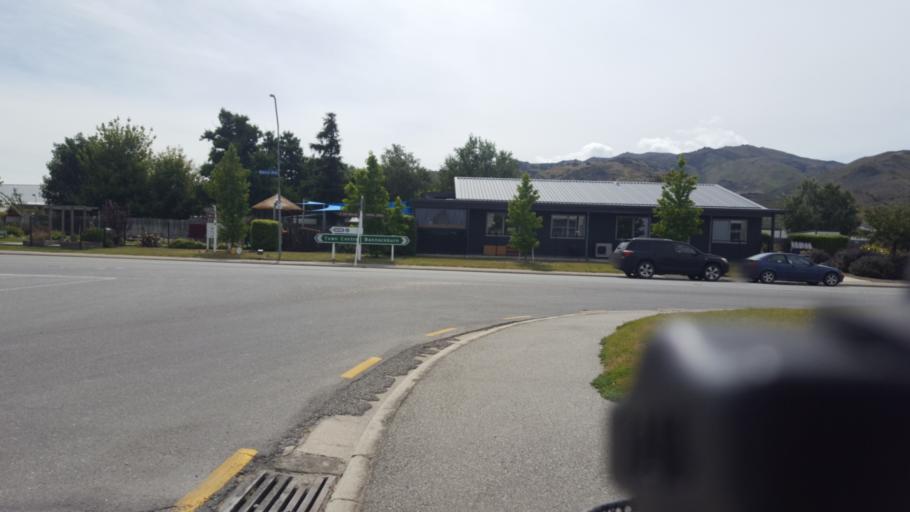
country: NZ
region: Otago
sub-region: Queenstown-Lakes District
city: Wanaka
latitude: -45.0495
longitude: 169.1946
